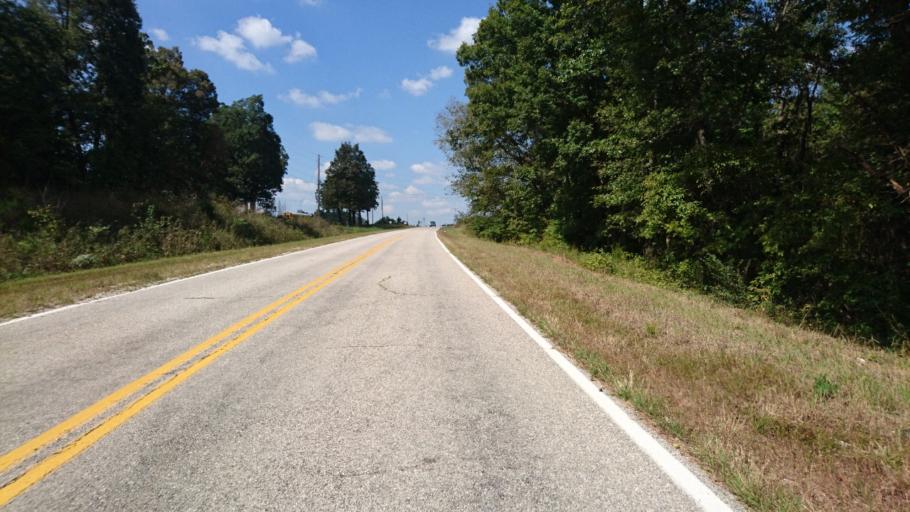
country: US
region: Missouri
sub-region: Pulaski County
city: Richland
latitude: 37.7530
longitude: -92.5031
